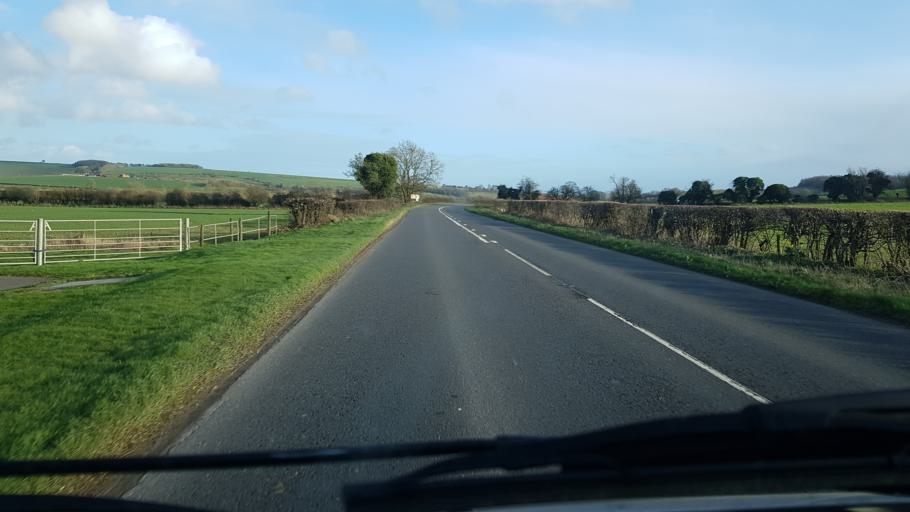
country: GB
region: England
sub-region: Wiltshire
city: Collingbourne Kingston
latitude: 51.3184
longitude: -1.6692
